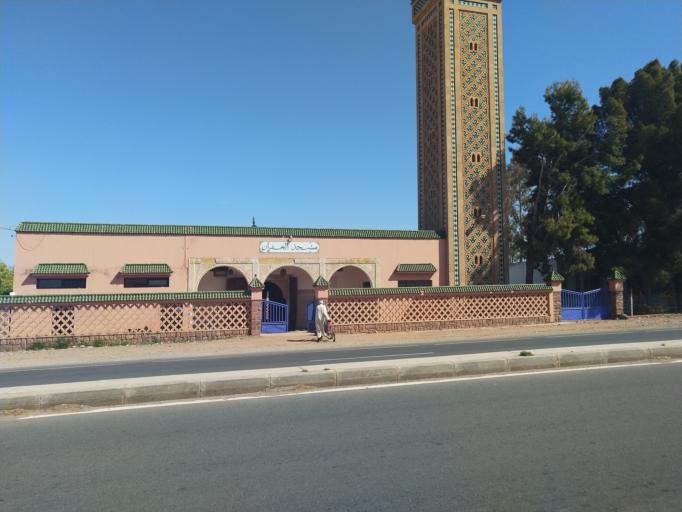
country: MA
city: Sidi Abdallah Ghiat
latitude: 31.5655
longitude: -7.7225
